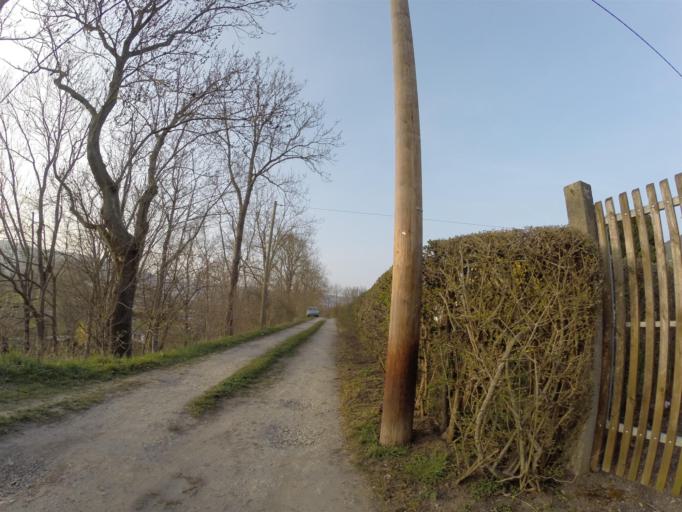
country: DE
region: Thuringia
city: Jena
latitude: 50.9364
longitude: 11.6096
